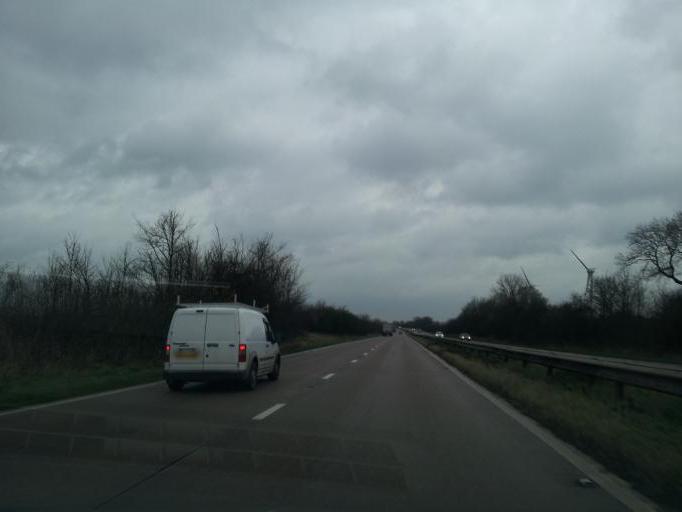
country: GB
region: England
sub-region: Leicestershire
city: Grimston
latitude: 52.8046
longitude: -1.0406
